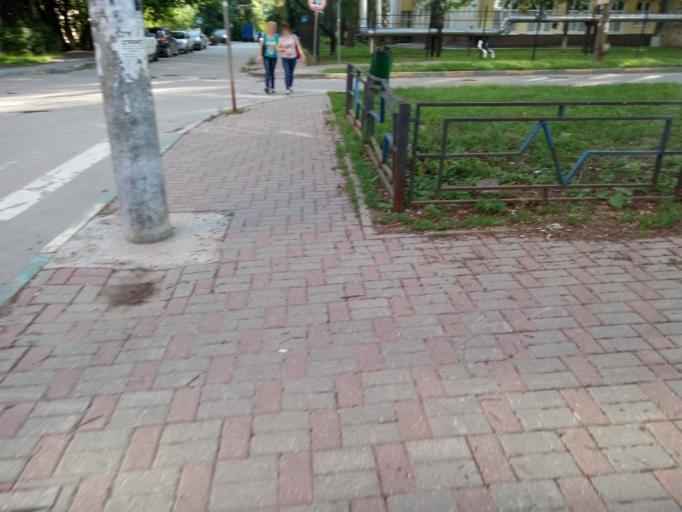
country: RU
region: Nizjnij Novgorod
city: Nizhniy Novgorod
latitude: 56.2698
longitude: 43.9810
